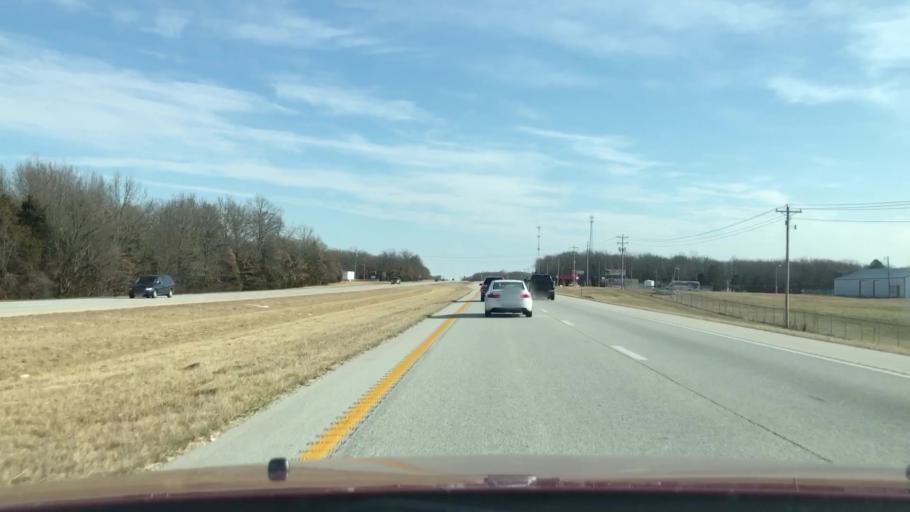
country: US
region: Missouri
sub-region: Webster County
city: Rogersville
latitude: 37.1158
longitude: -93.0276
